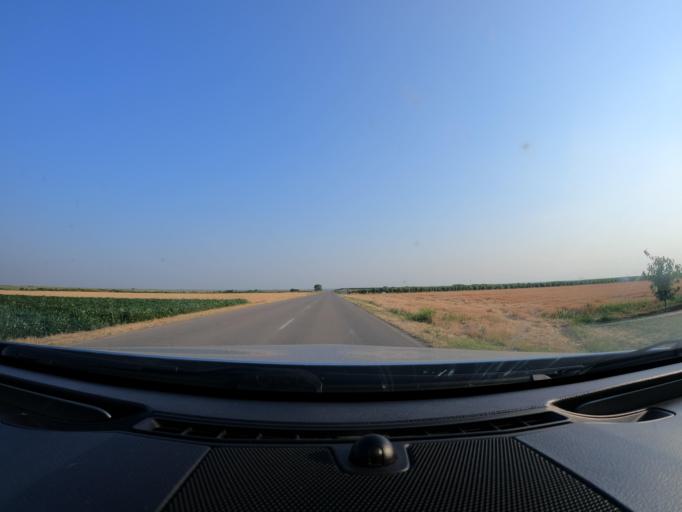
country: RS
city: Vrdnik
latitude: 45.0540
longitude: 19.7657
